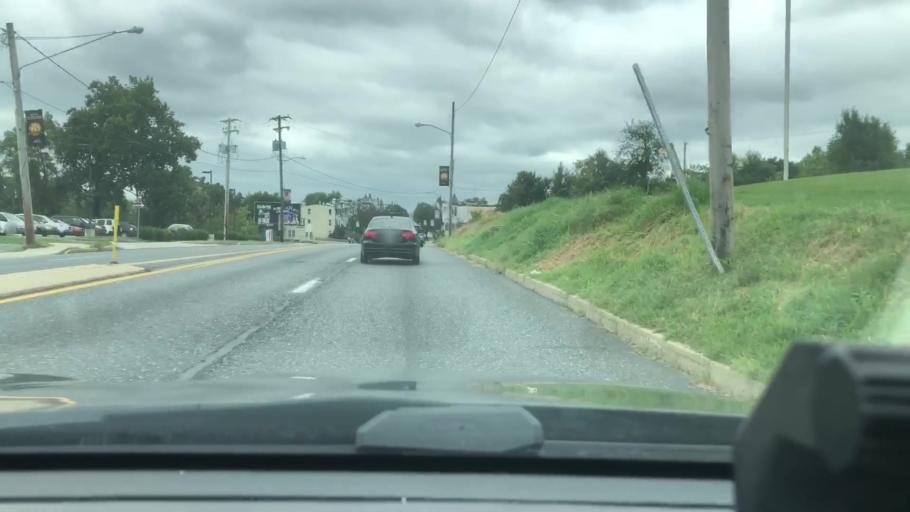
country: US
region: Pennsylvania
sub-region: Lehigh County
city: Allentown
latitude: 40.6182
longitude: -75.4794
